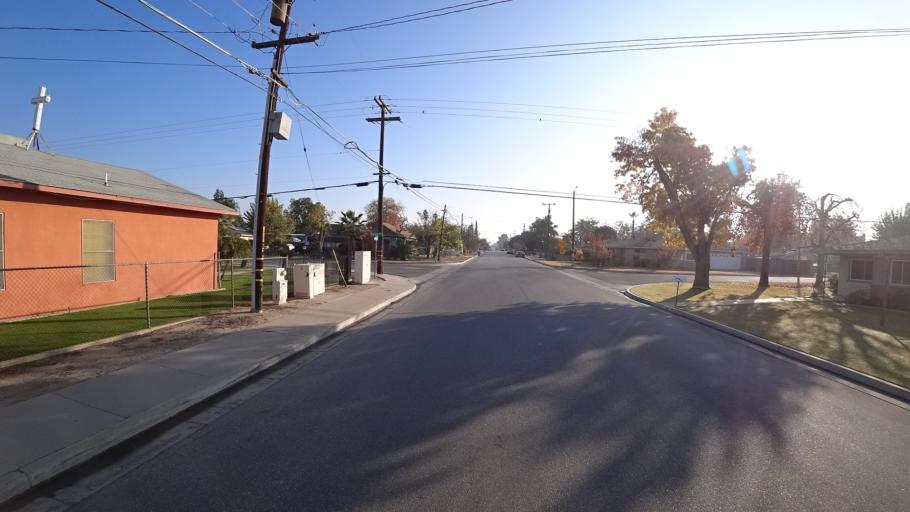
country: US
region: California
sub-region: Kern County
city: Greenacres
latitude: 35.3797
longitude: -119.1174
